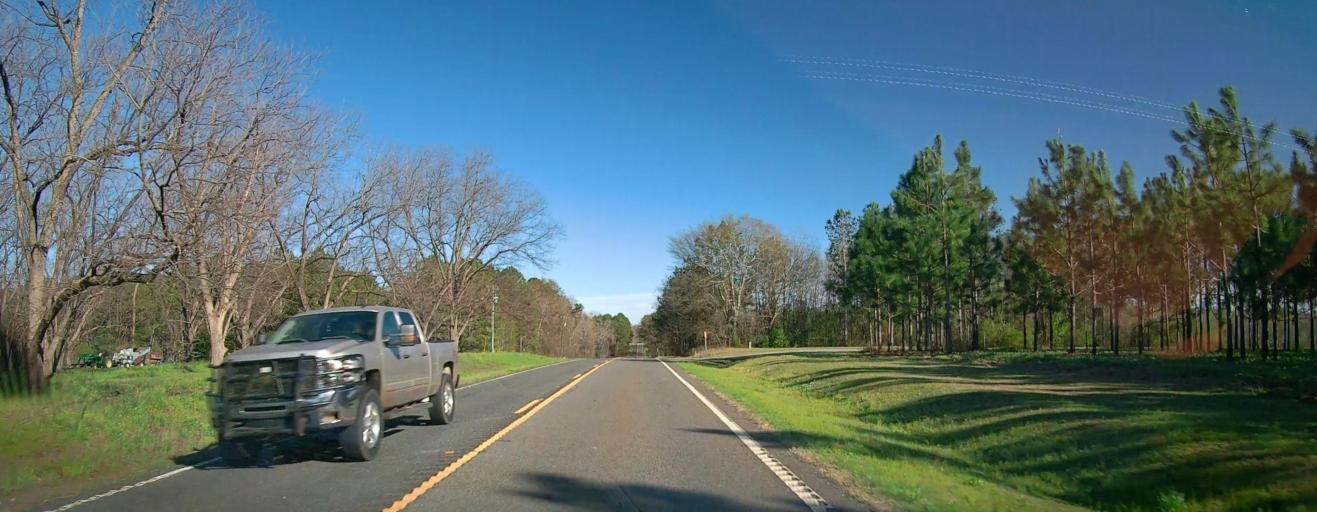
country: US
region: Georgia
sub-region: Macon County
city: Marshallville
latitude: 32.4447
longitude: -83.8983
